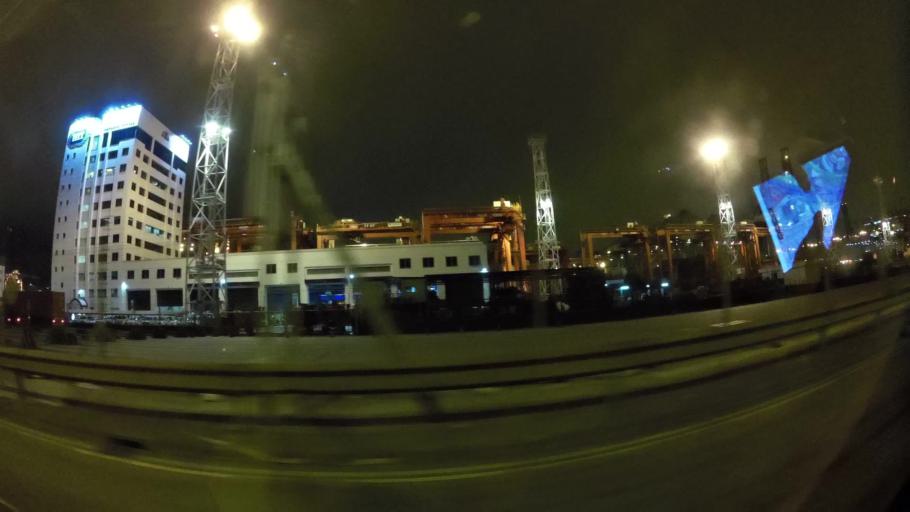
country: HK
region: Sham Shui Po
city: Sham Shui Po
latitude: 22.3353
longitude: 114.1321
